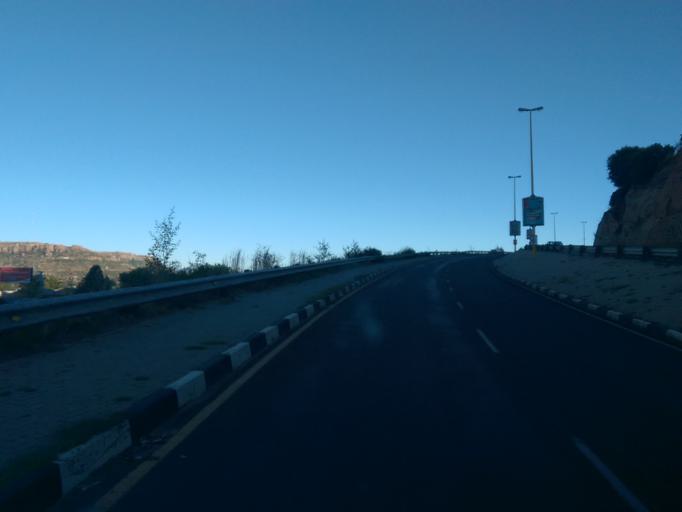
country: LS
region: Maseru
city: Maseru
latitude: -29.3179
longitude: 27.4932
